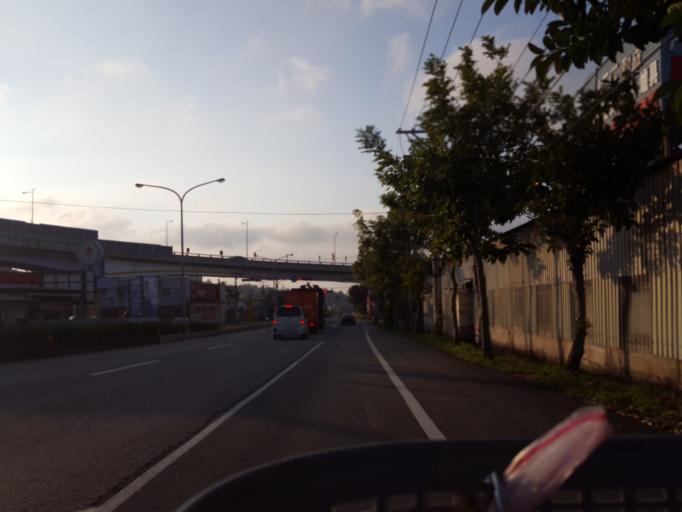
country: TW
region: Taiwan
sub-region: Hsinchu
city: Zhubei
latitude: 24.8803
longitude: 121.0367
